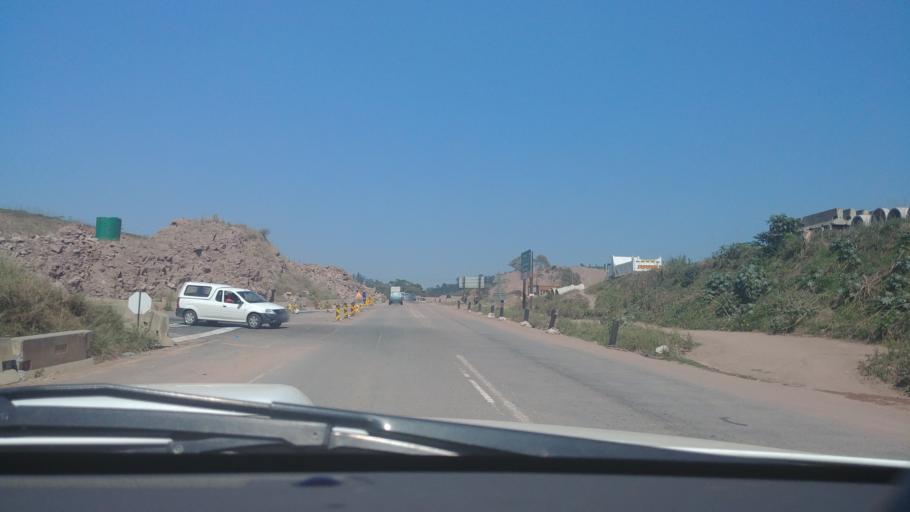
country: ZA
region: KwaZulu-Natal
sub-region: eThekwini Metropolitan Municipality
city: Mpumalanga
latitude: -29.7581
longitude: 30.6657
